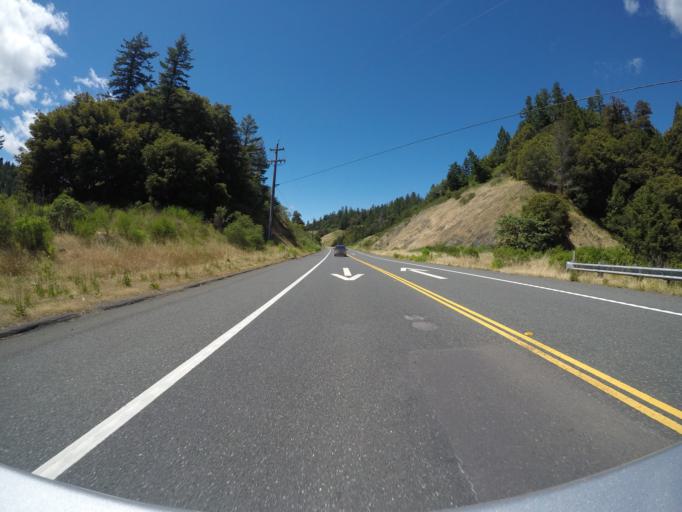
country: US
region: California
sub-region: Humboldt County
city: Redway
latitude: 39.9294
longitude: -123.7620
